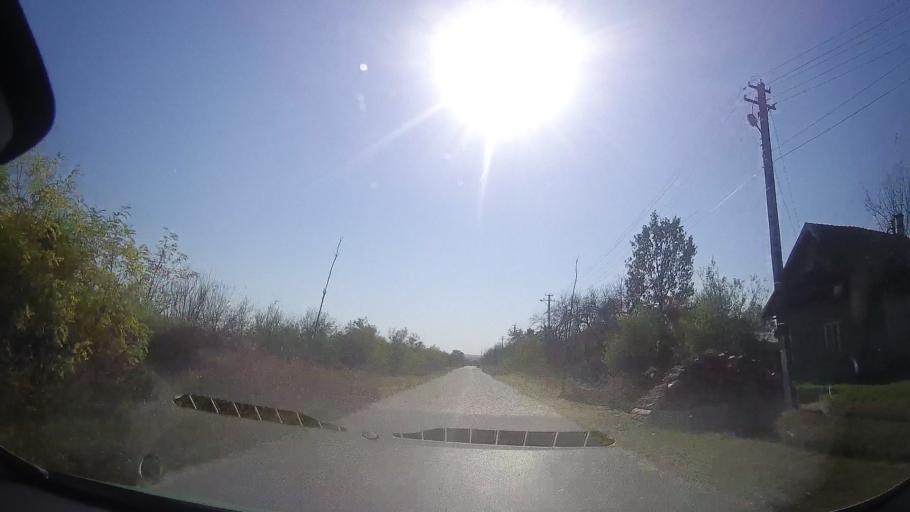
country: RO
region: Timis
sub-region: Comuna Ghizela
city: Ghizela
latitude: 45.8271
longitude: 21.7500
